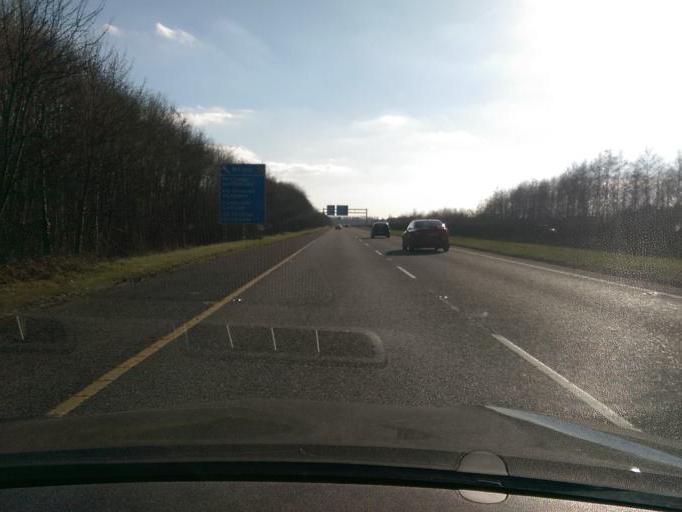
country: IE
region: Leinster
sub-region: Kildare
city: Kilcullen
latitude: 53.1828
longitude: -6.7363
